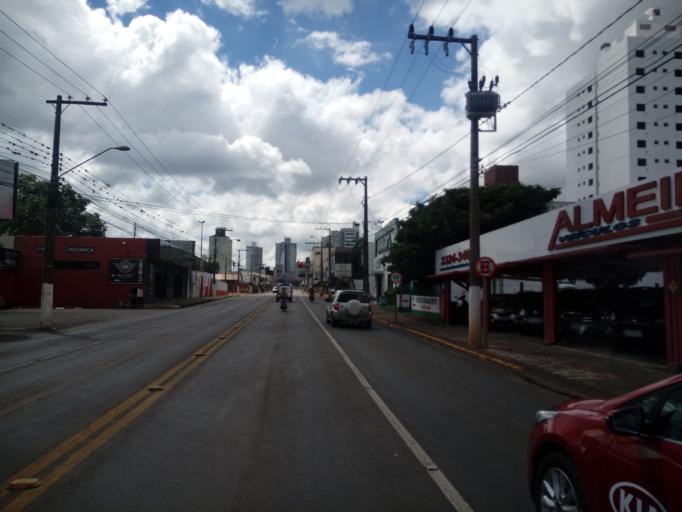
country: BR
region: Santa Catarina
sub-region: Chapeco
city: Chapeco
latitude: -27.0931
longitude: -52.6223
